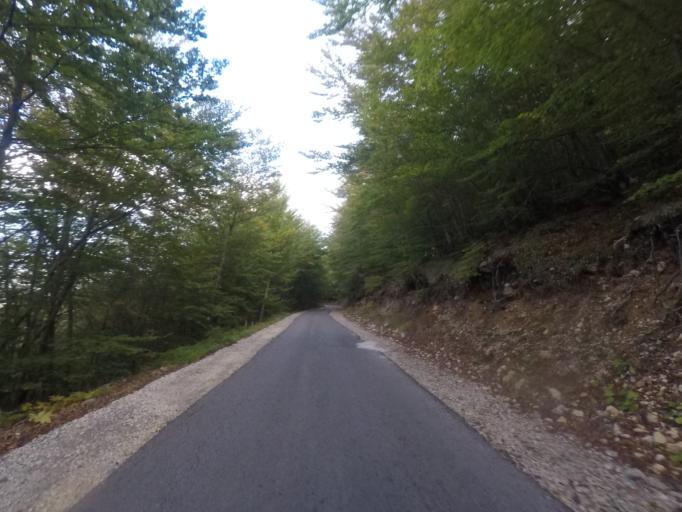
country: ME
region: Kotor
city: Kotor
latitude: 42.4205
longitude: 18.8036
